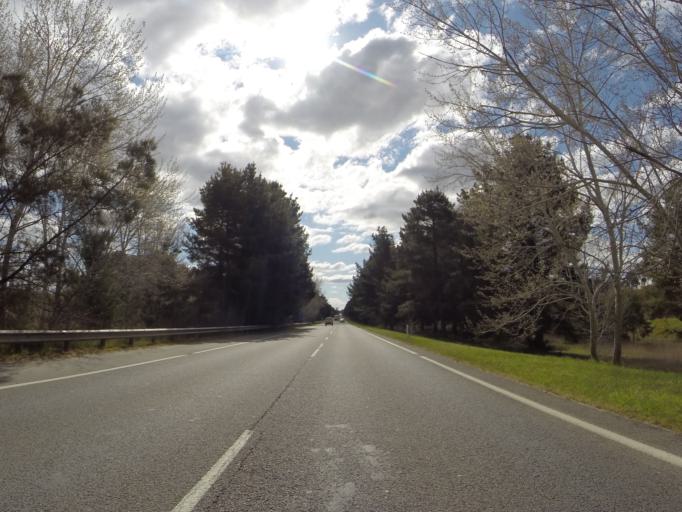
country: AU
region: Australian Capital Territory
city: Belconnen
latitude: -35.2002
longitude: 149.0929
